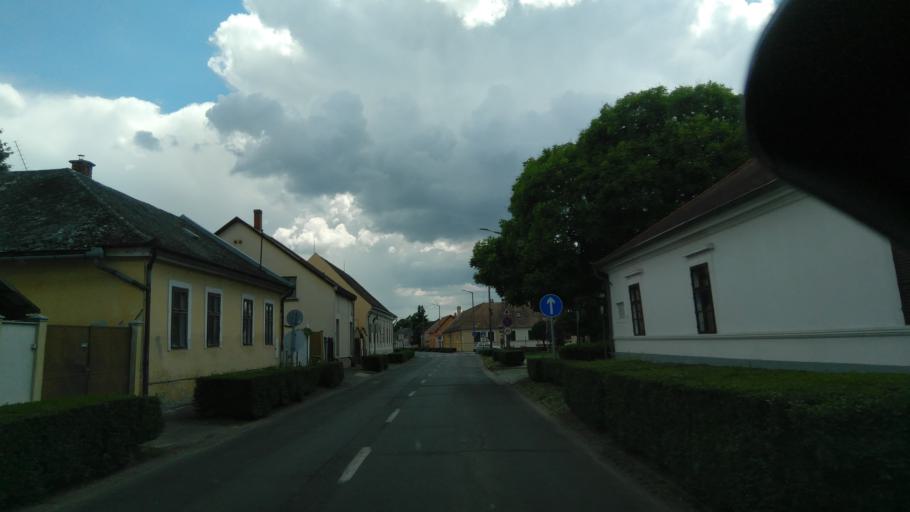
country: HU
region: Bekes
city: Gyula
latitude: 46.6471
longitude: 21.2682
